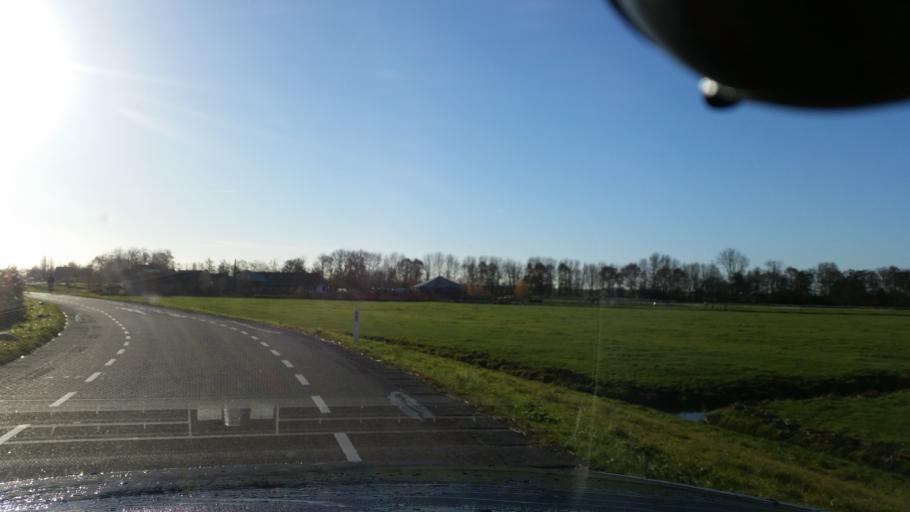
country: NL
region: North Holland
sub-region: Gemeente Ouder-Amstel
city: Ouderkerk aan de Amstel
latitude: 52.2784
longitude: 4.9257
